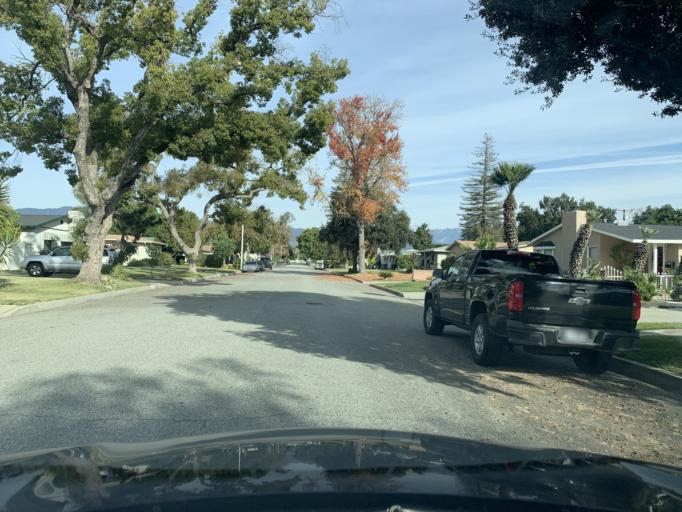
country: US
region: California
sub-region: Los Angeles County
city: West Covina
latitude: 34.0764
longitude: -117.9310
